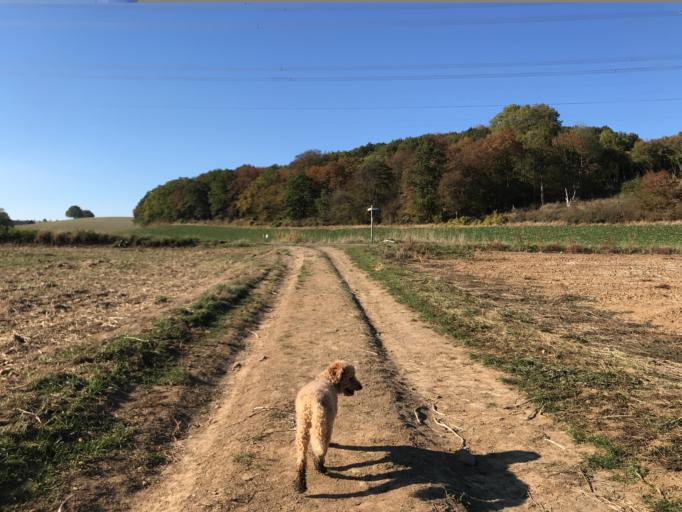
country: DE
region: Rheinland-Pfalz
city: Wolken
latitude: 50.3357
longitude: 7.4425
